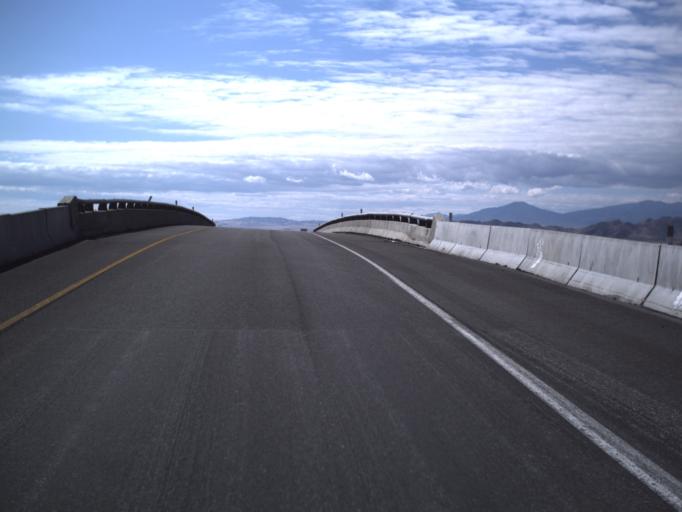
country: US
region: Utah
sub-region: Tooele County
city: Wendover
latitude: 40.7467
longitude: -114.0170
